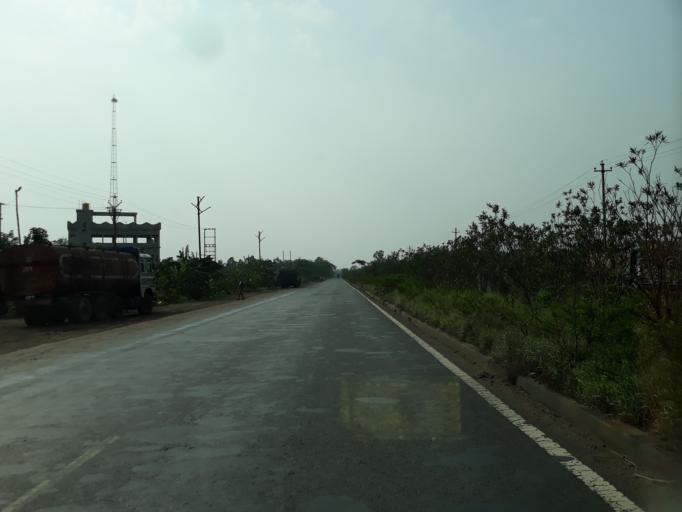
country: IN
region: West Bengal
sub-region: Purba Medinipur
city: Mahishadal
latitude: 22.1655
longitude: 87.9452
